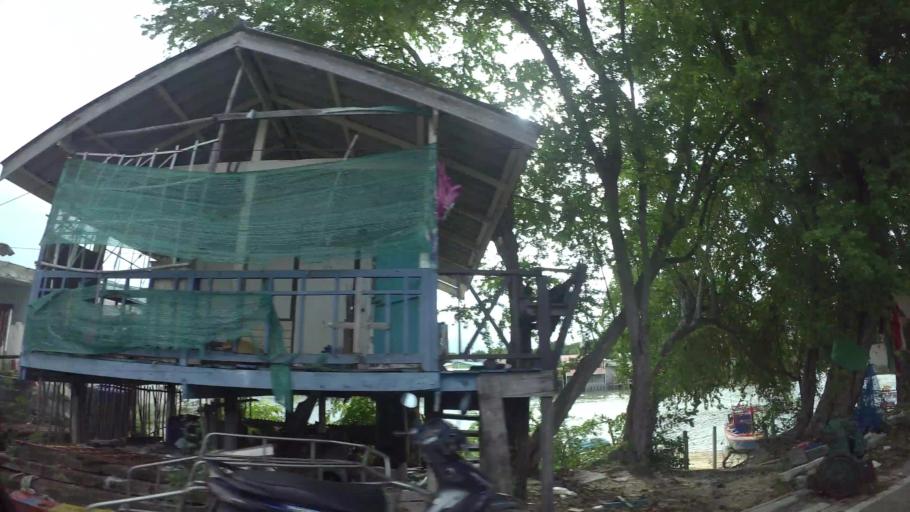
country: TH
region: Rayong
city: Rayong
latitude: 12.6604
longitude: 101.2787
